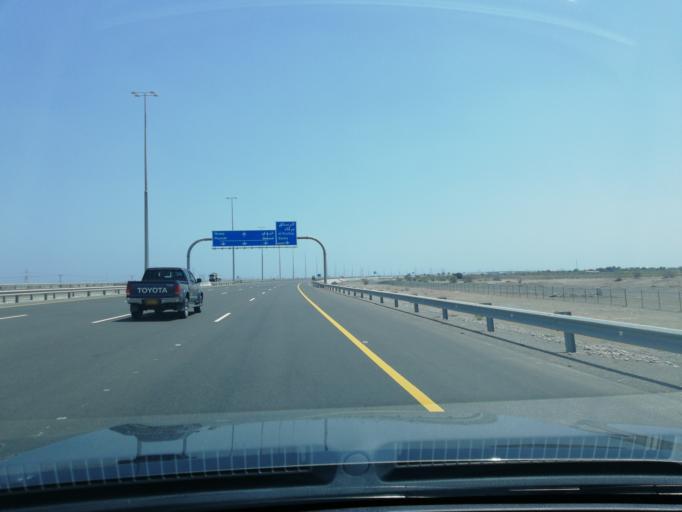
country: OM
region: Al Batinah
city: Barka'
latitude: 23.6271
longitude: 57.8489
